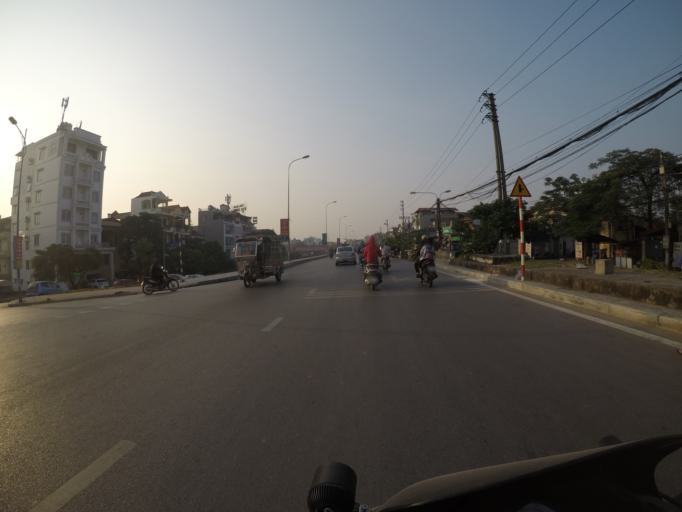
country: VN
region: Ha Noi
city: Hoan Kiem
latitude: 21.0436
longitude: 105.8655
